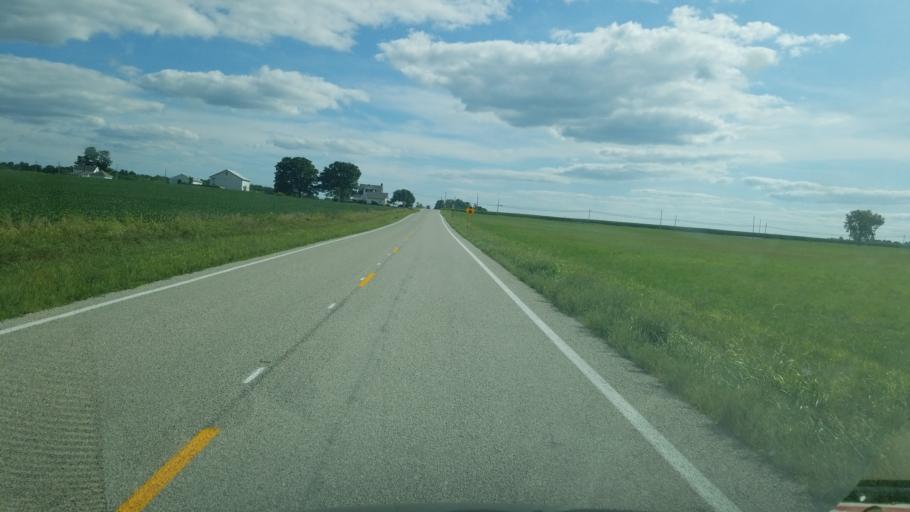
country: US
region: Ohio
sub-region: Champaign County
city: Saint Paris
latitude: 40.2208
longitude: -83.9409
